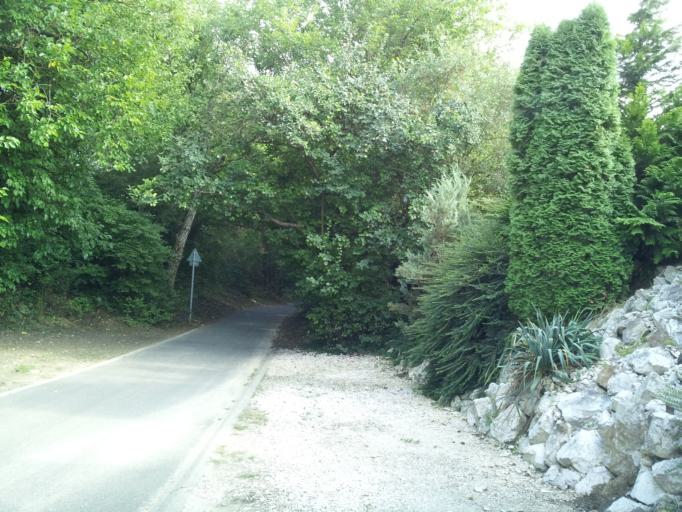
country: HU
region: Pest
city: Vac
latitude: 47.8034
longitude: 19.1008
